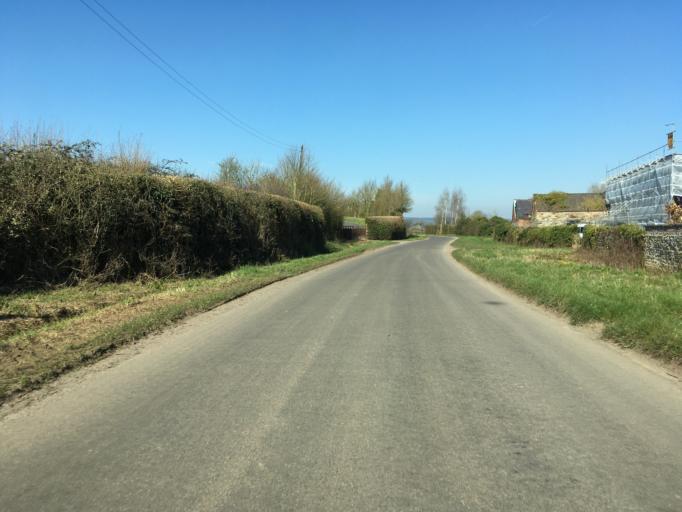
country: GB
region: England
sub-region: Gloucestershire
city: Berkeley
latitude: 51.6794
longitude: -2.4871
